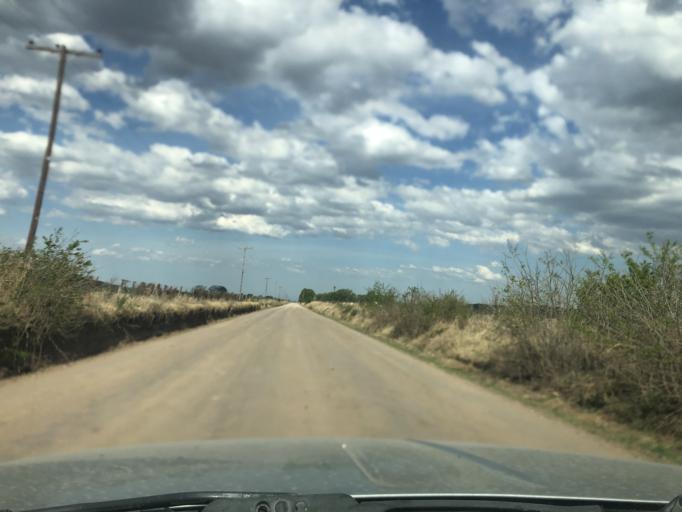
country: AR
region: Cordoba
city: Jesus Maria
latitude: -31.0122
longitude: -64.1475
